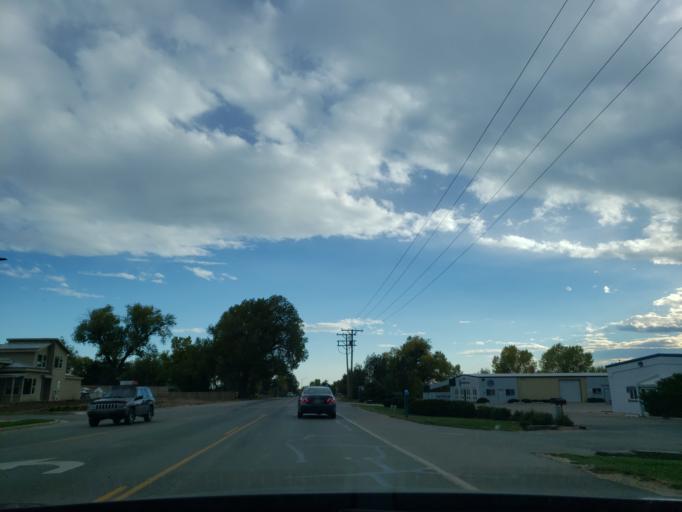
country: US
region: Colorado
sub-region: Larimer County
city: Fort Collins
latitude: 40.5901
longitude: -105.0295
